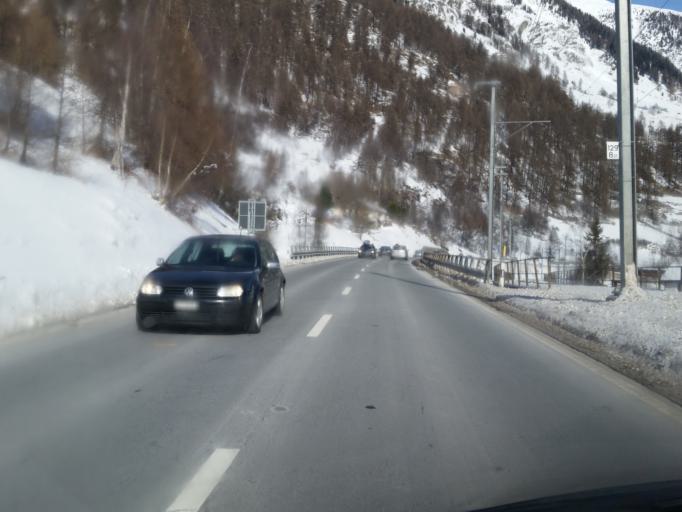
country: CH
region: Grisons
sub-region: Inn District
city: Zernez
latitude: 46.7675
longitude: 10.1089
